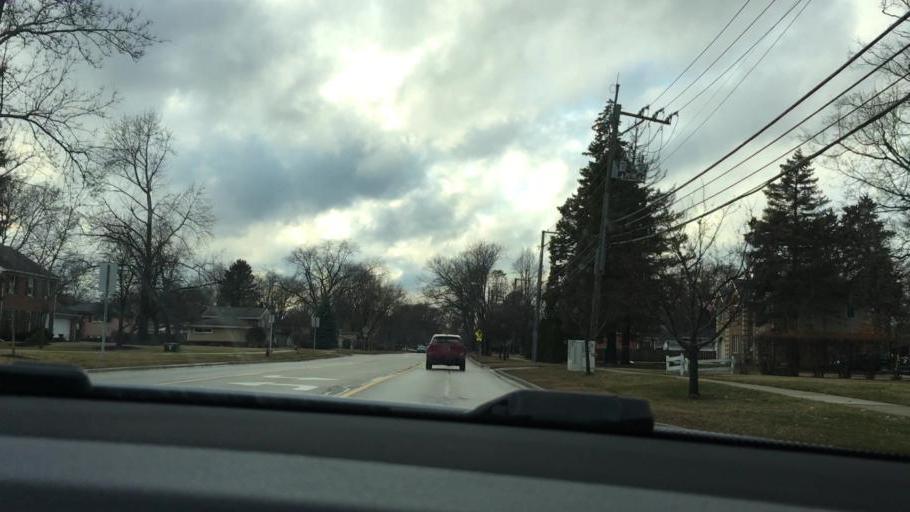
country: US
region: Illinois
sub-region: Cook County
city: Arlington Heights
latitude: 42.0882
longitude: -87.9600
